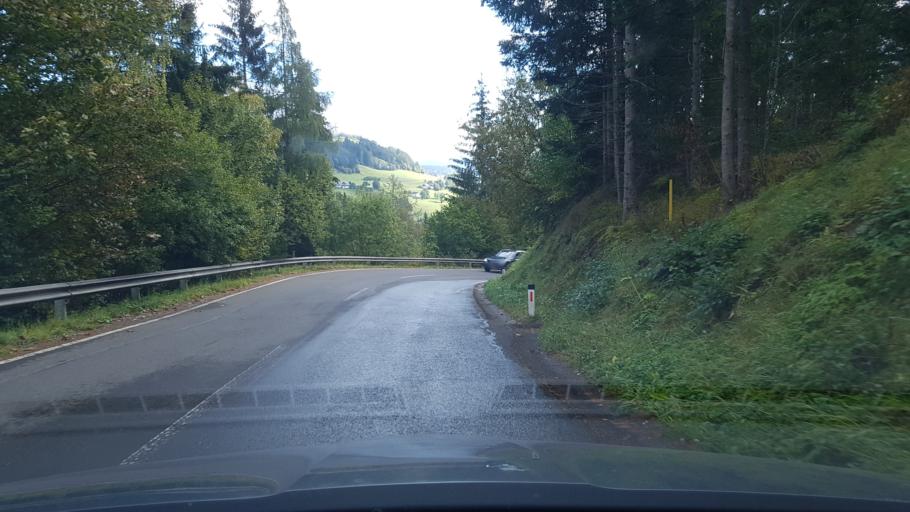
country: AT
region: Styria
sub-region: Politischer Bezirk Murau
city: Schoder
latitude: 47.1920
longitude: 14.1236
